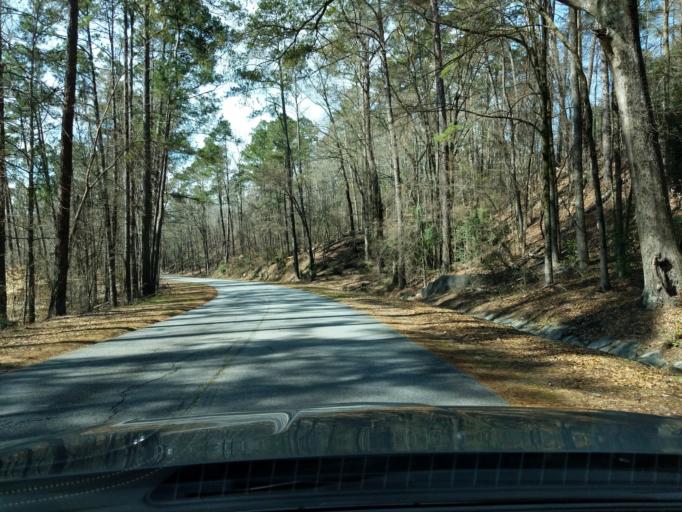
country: US
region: Georgia
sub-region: Columbia County
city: Evans
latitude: 33.6622
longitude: -82.1890
